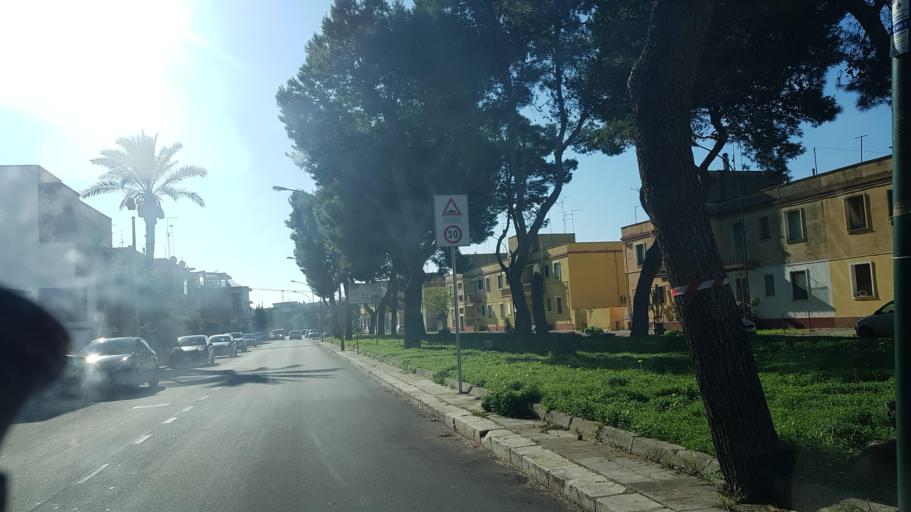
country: IT
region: Apulia
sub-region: Provincia di Lecce
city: Campi Salentina
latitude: 40.4037
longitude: 18.0212
